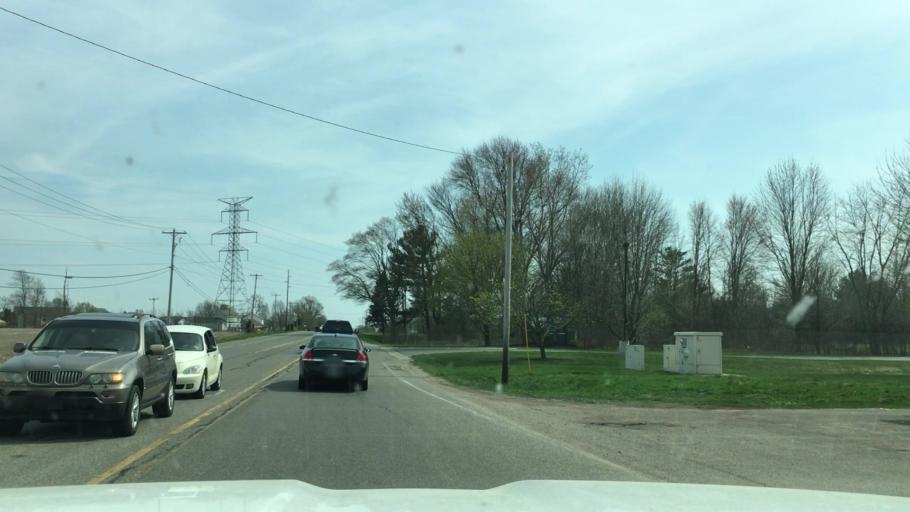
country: US
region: Michigan
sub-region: Ottawa County
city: Hudsonville
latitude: 42.8850
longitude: -85.9015
